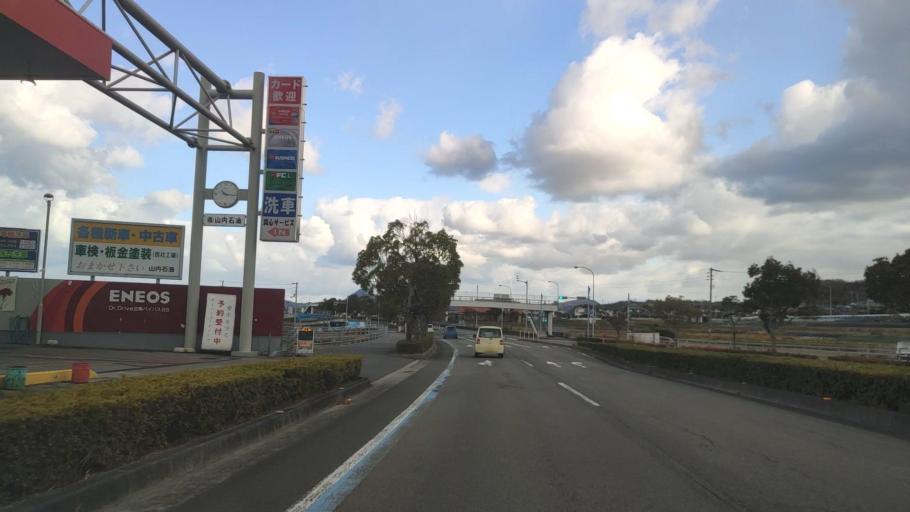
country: JP
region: Ehime
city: Hojo
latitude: 33.9370
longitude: 132.7726
